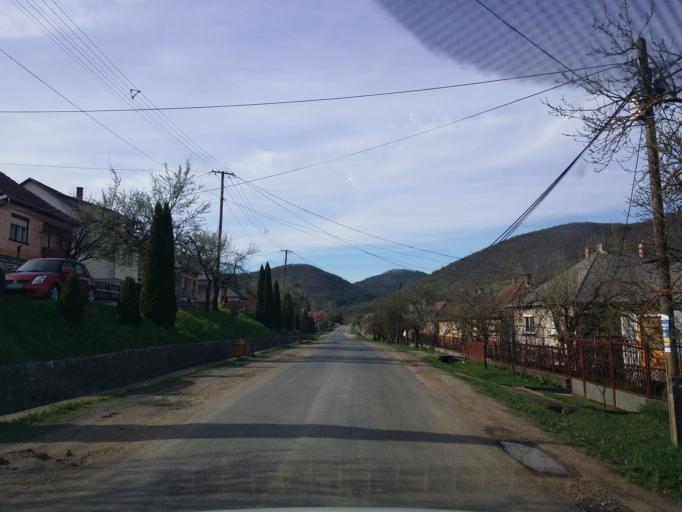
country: HU
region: Borsod-Abauj-Zemplen
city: Szendro
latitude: 48.5162
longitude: 20.6795
